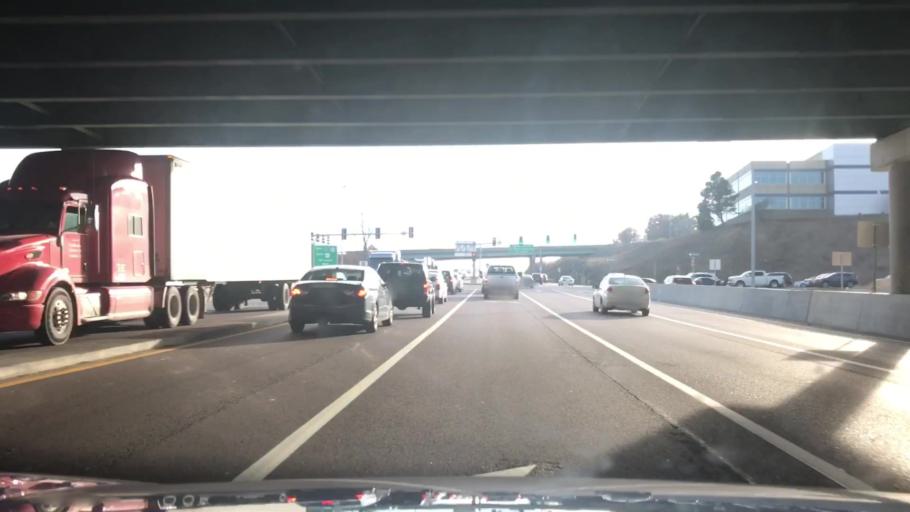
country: US
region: Missouri
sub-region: Saint Louis County
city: Manchester
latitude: 38.6424
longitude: -90.5104
